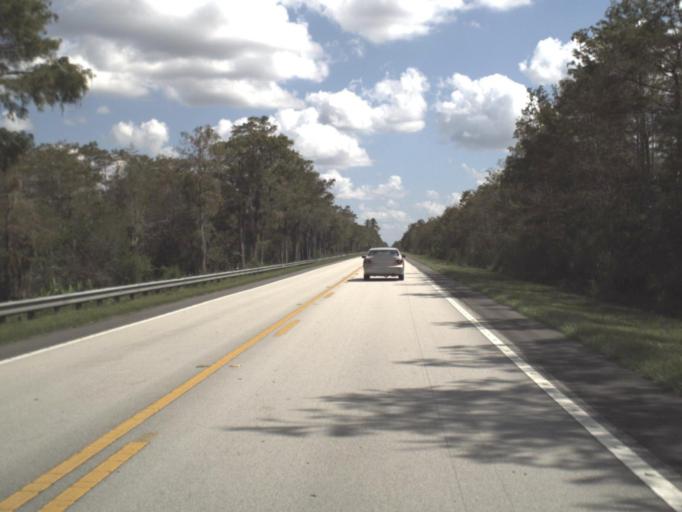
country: US
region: Florida
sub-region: Miami-Dade County
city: Kendall West
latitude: 25.8427
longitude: -80.9165
